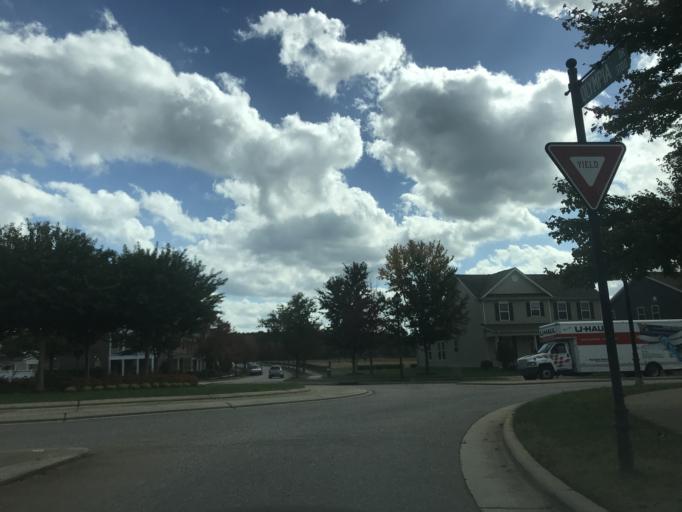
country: US
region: North Carolina
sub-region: Wake County
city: Raleigh
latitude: 35.7359
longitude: -78.6587
